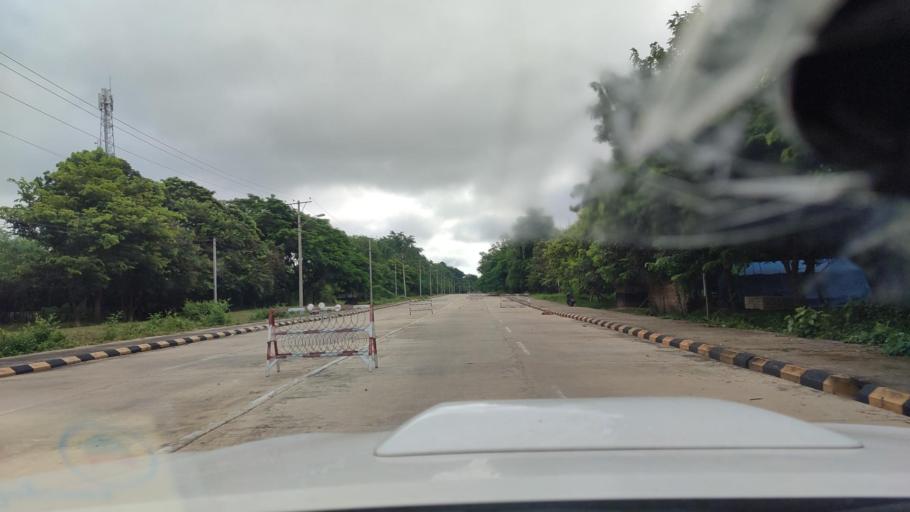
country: MM
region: Mandalay
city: Nay Pyi Taw
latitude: 19.7609
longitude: 96.0725
